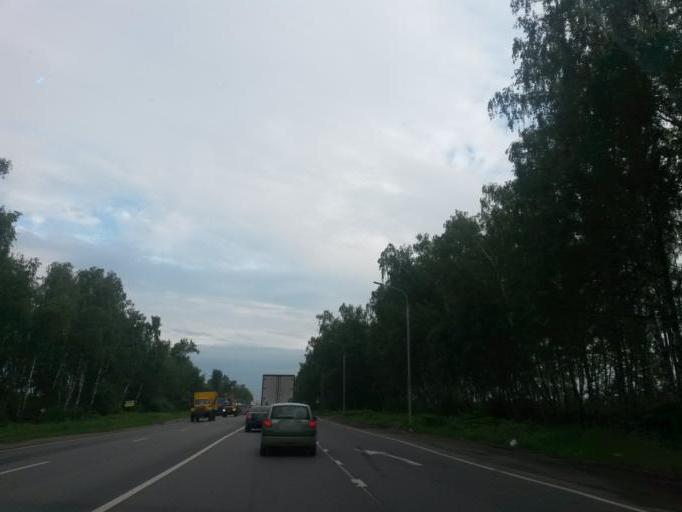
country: RU
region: Moskovskaya
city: Belyye Stolby
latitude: 55.2804
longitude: 37.8238
